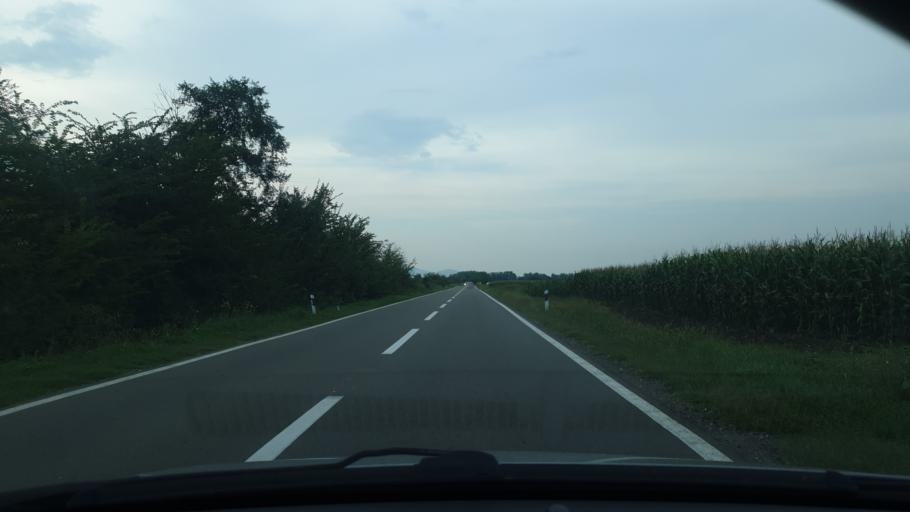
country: RS
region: Central Serbia
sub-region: Sumadijski Okrug
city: Topola
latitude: 44.3450
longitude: 20.6810
